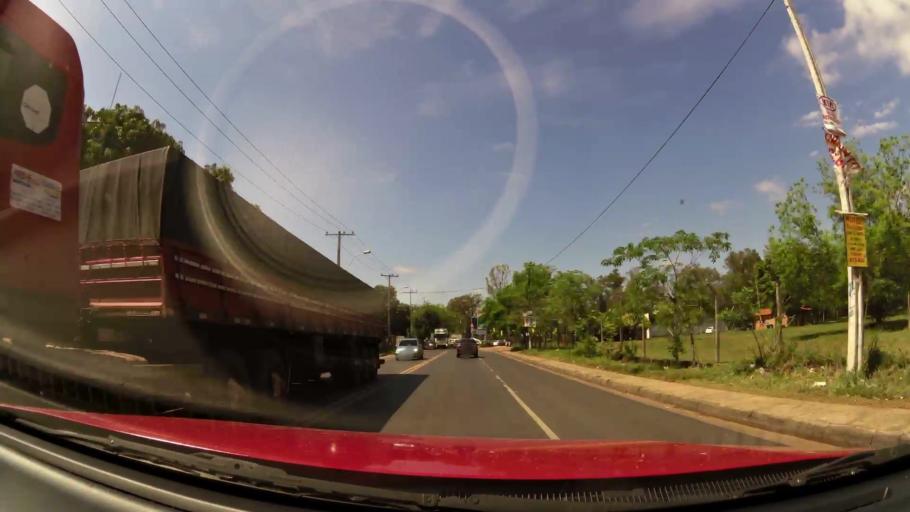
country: PY
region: Central
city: San Lorenzo
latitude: -25.3357
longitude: -57.5105
